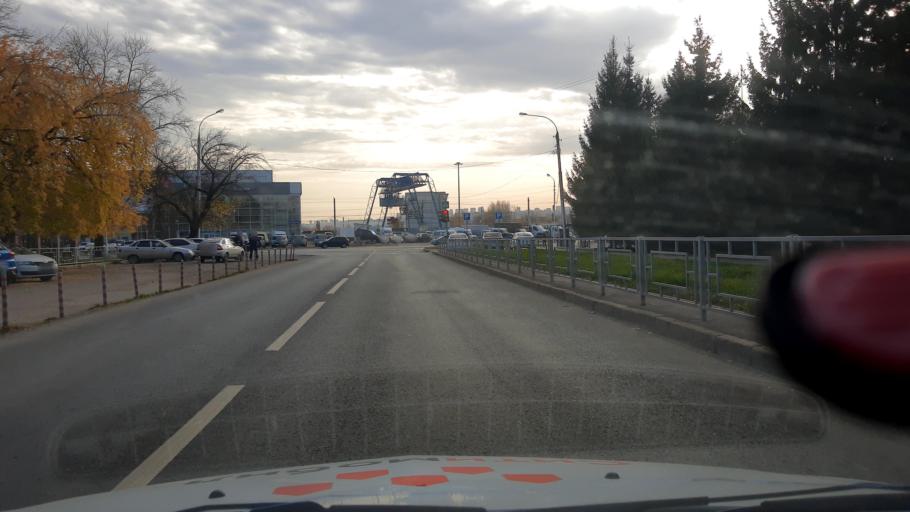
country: RU
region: Bashkortostan
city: Ufa
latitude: 54.8113
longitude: 56.0813
